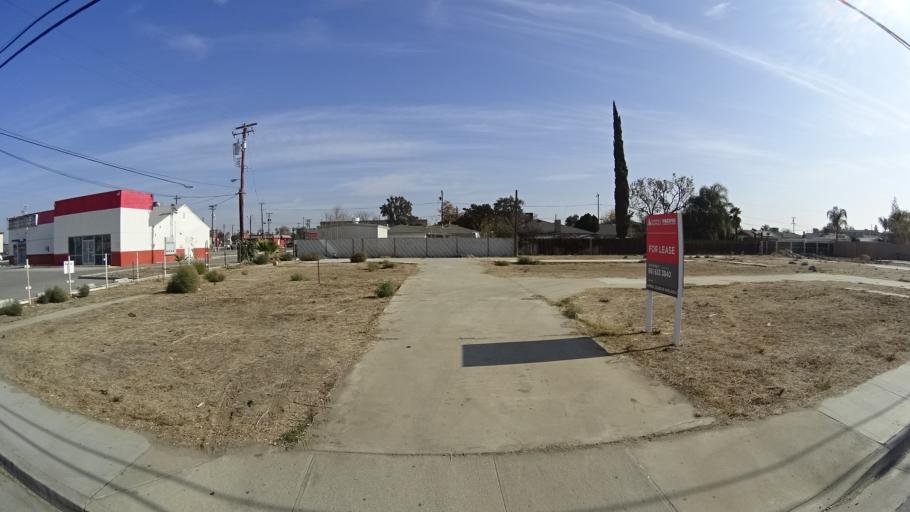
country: US
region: California
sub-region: Kern County
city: Greenacres
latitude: 35.3828
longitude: -119.1099
